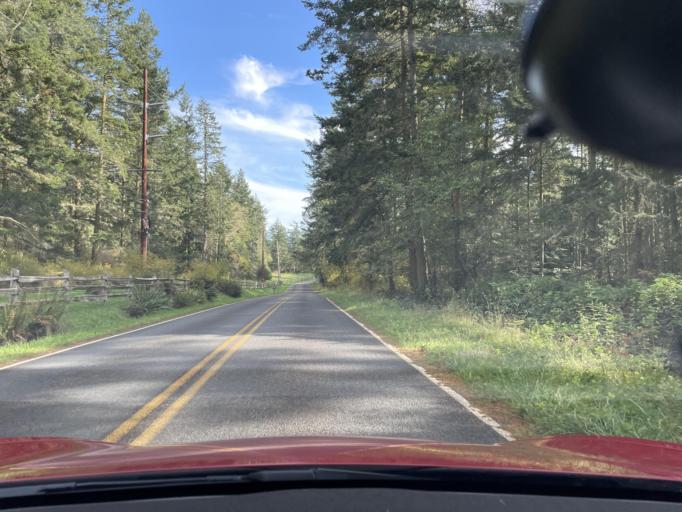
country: US
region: Washington
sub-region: San Juan County
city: Friday Harbor
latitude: 48.5186
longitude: -122.9915
